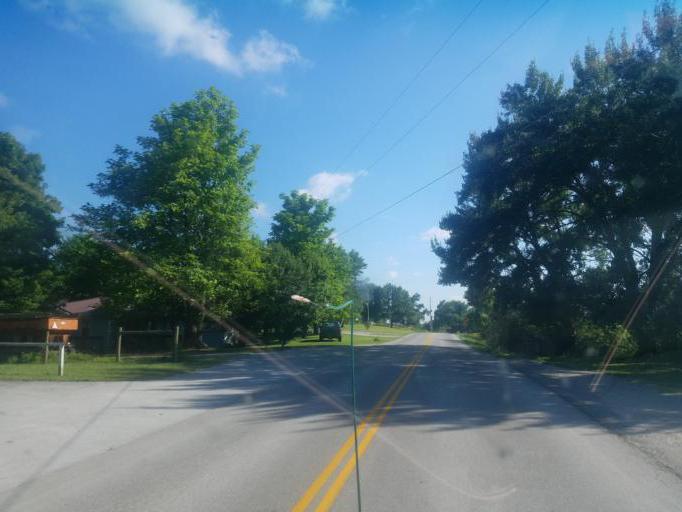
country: US
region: Kentucky
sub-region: Hart County
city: Munfordville
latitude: 37.2862
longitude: -85.9909
